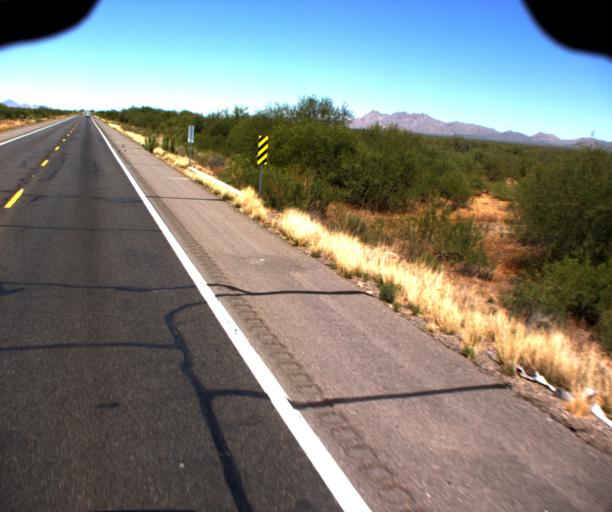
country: US
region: Arizona
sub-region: Yavapai County
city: Congress
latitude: 34.1131
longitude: -112.9357
